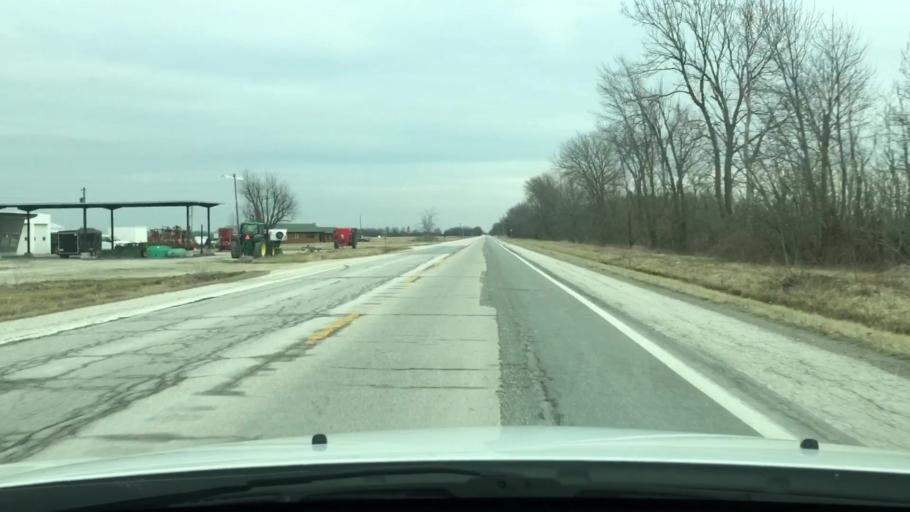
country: US
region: Missouri
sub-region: Audrain County
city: Vandalia
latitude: 39.3188
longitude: -91.4659
